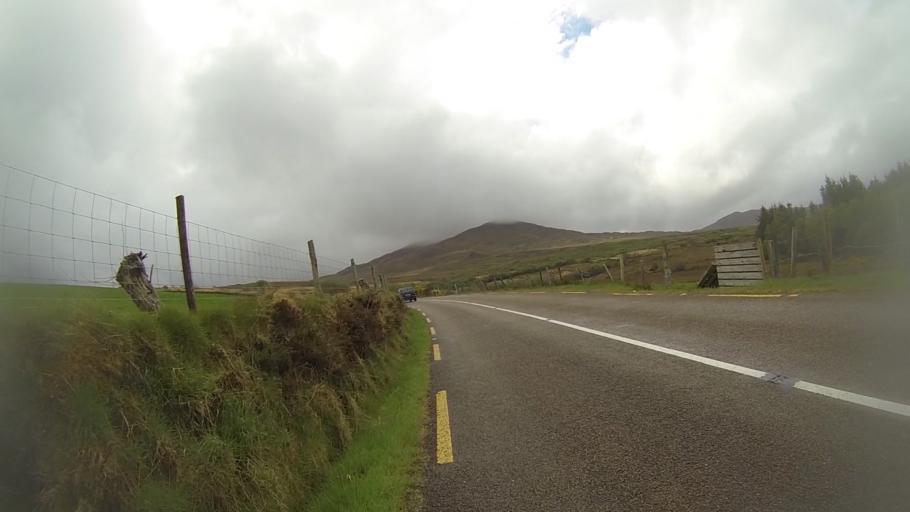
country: IE
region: Munster
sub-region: Ciarrai
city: Kenmare
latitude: 51.8839
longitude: -9.7860
